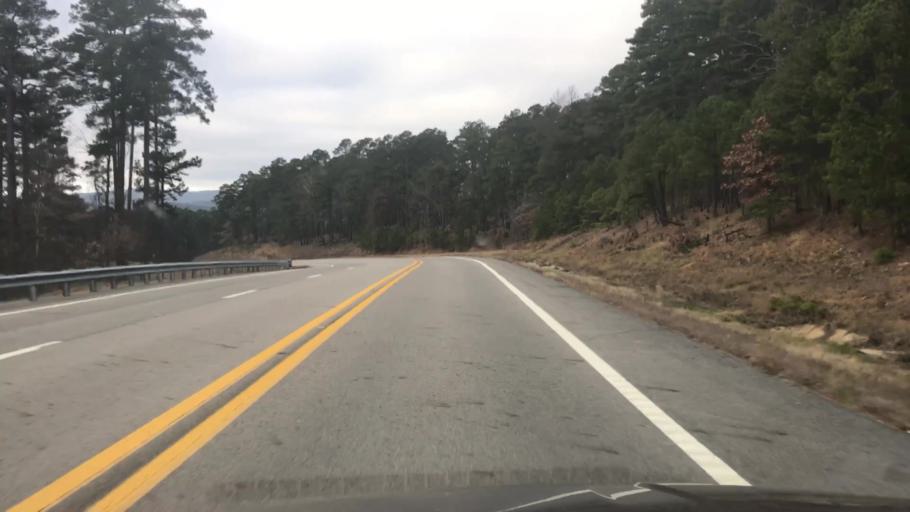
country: US
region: Arkansas
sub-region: Montgomery County
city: Mount Ida
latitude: 34.6831
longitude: -93.7930
